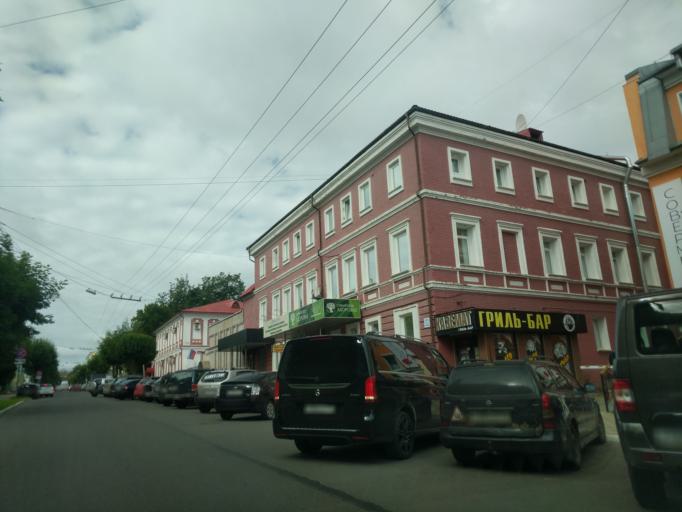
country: RU
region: Kirov
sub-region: Kirovo-Chepetskiy Rayon
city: Kirov
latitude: 58.6037
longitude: 49.6755
